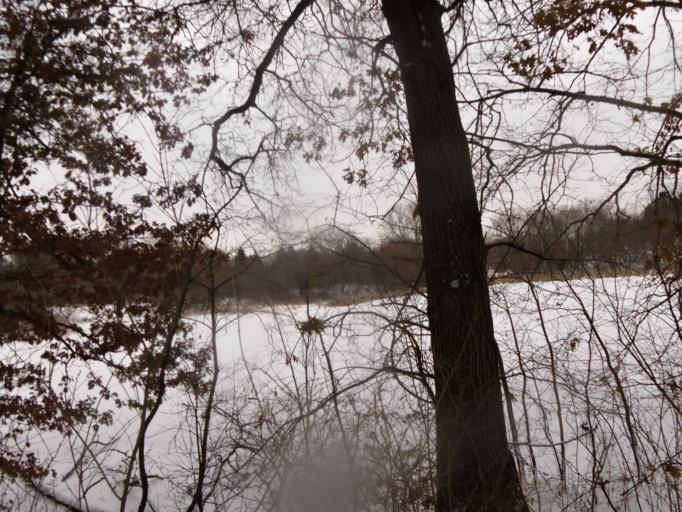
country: US
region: Minnesota
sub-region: Dakota County
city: Inver Grove Heights
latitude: 44.8625
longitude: -93.0753
